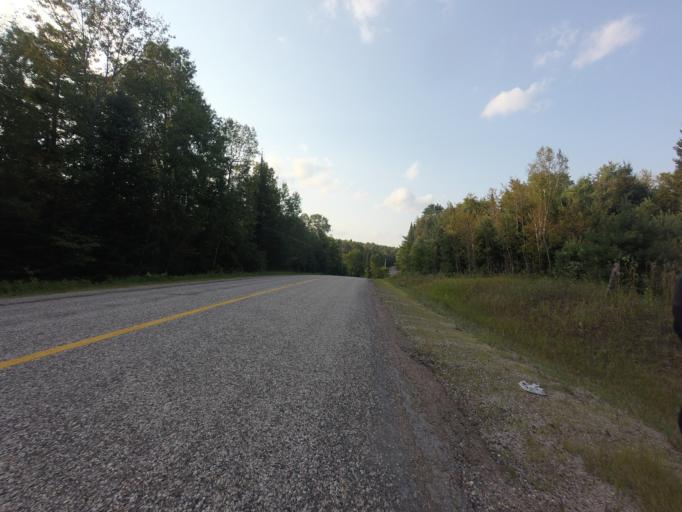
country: CA
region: Ontario
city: Renfrew
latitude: 44.9771
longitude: -76.7402
